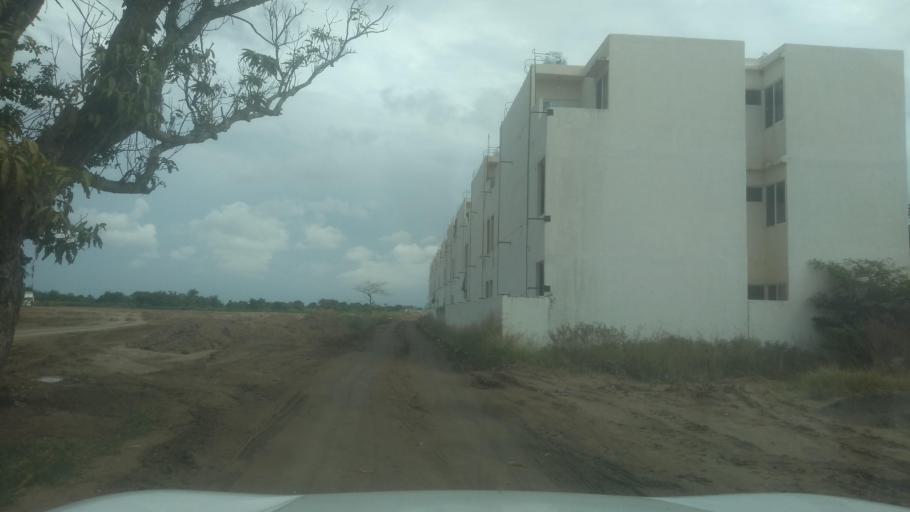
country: MX
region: Veracruz
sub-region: Medellin
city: Fraccionamiento Arboledas San Ramon
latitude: 19.0940
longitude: -96.1711
